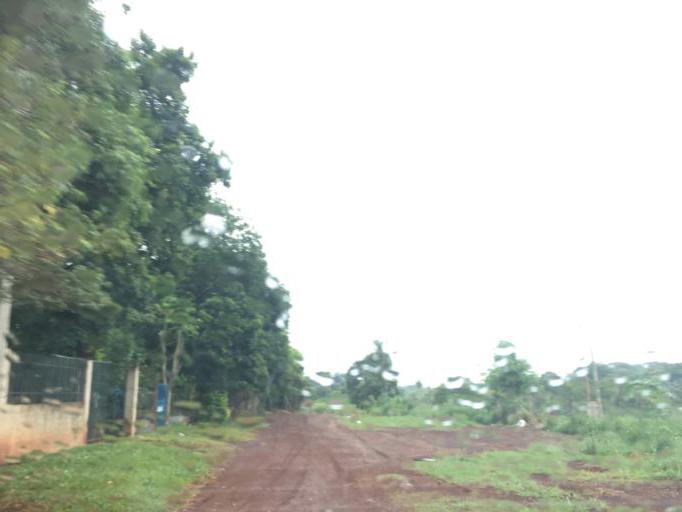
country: PY
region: Alto Parana
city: Ciudad del Este
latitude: -25.4353
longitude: -54.6542
